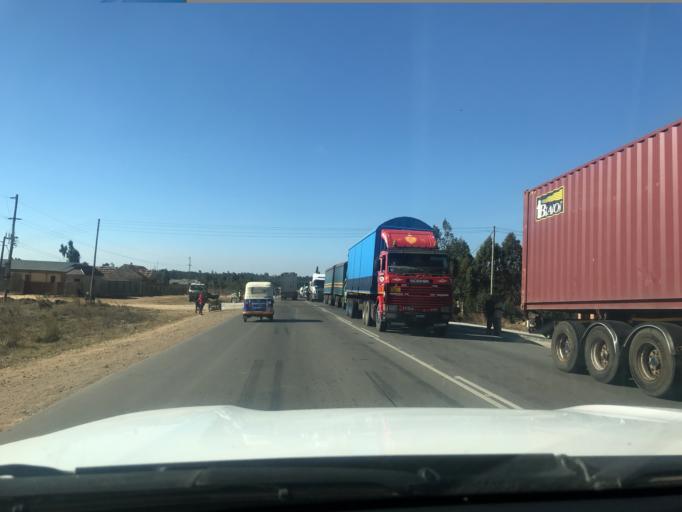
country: TZ
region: Njombe
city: Makumbako
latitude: -8.8147
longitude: 34.8416
